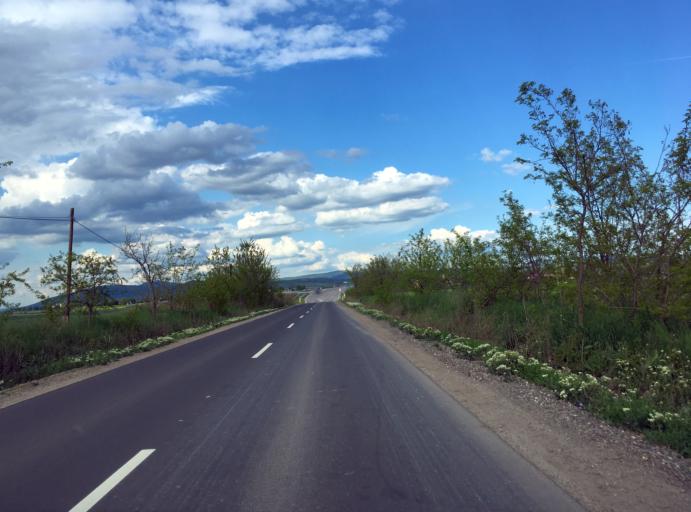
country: HU
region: Heves
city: Lorinci
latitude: 47.7285
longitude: 19.6614
